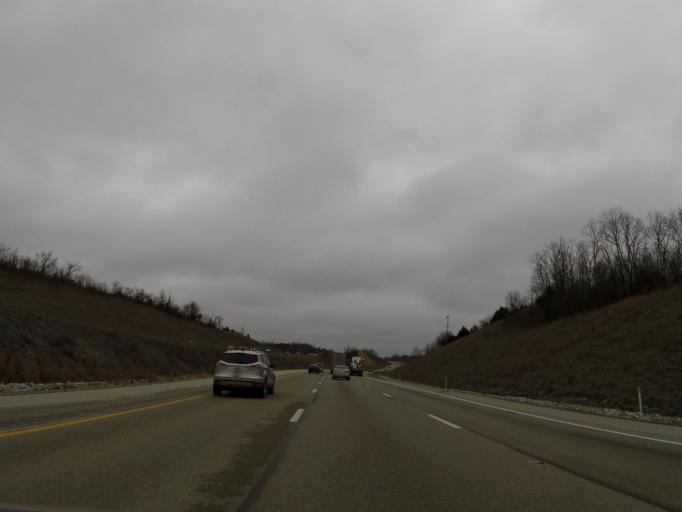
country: US
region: Kentucky
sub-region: Grant County
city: Williamstown
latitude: 38.5681
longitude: -84.5932
